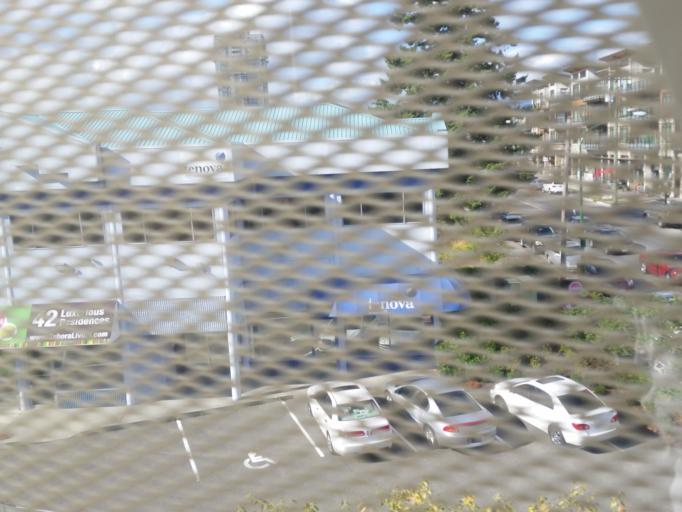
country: CA
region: British Columbia
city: Burnaby
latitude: 49.2202
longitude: -122.9888
